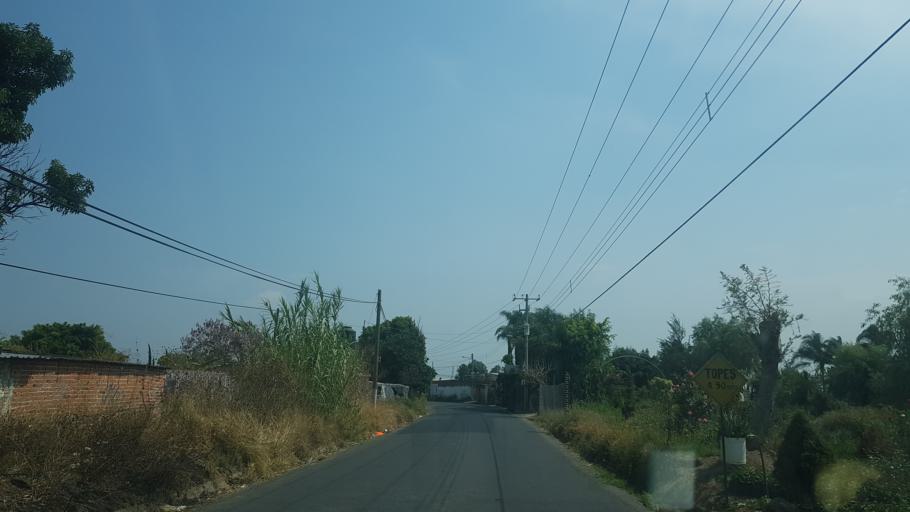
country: MX
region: Puebla
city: Atlixco
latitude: 18.9276
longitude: -98.4543
